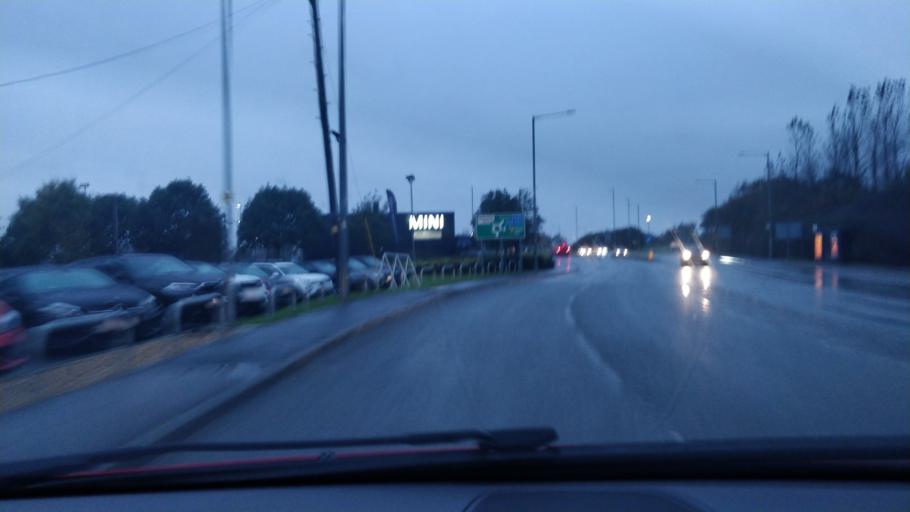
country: GB
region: England
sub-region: Lancashire
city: Poulton le Fylde
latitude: 53.7884
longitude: -2.9795
